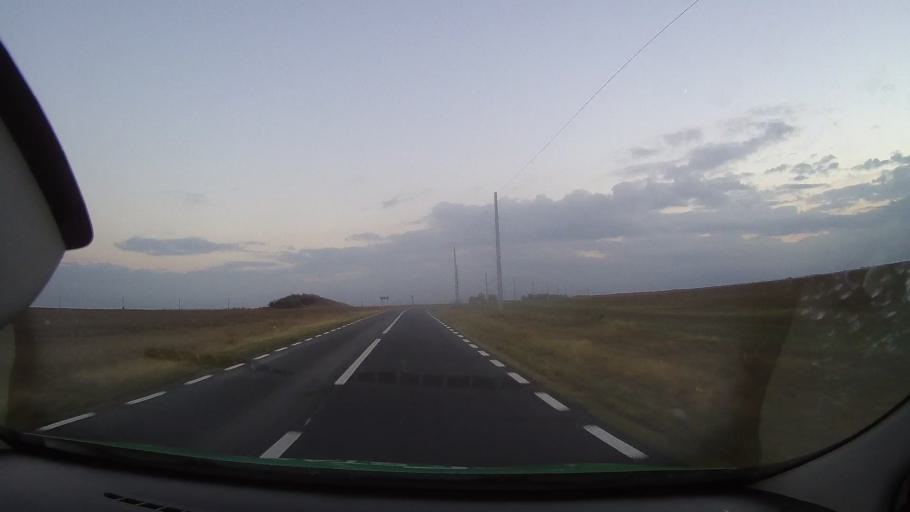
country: RO
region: Constanta
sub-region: Comuna Oltina
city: Oltina
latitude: 44.1330
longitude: 27.6681
